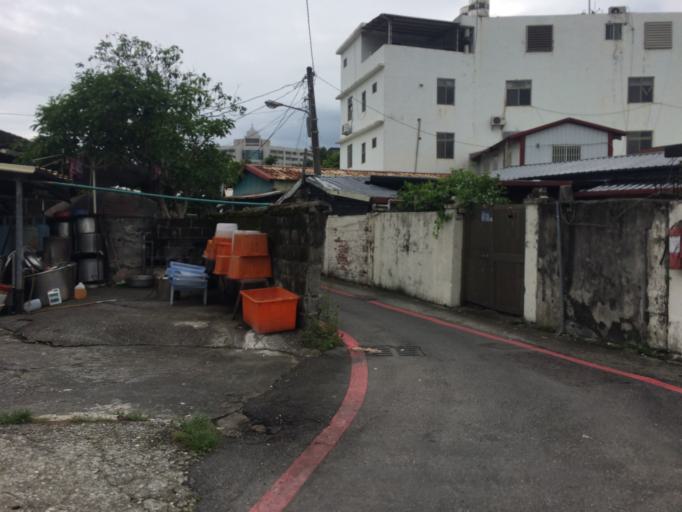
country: TW
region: Taiwan
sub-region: Hualien
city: Hualian
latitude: 23.9864
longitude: 121.6051
